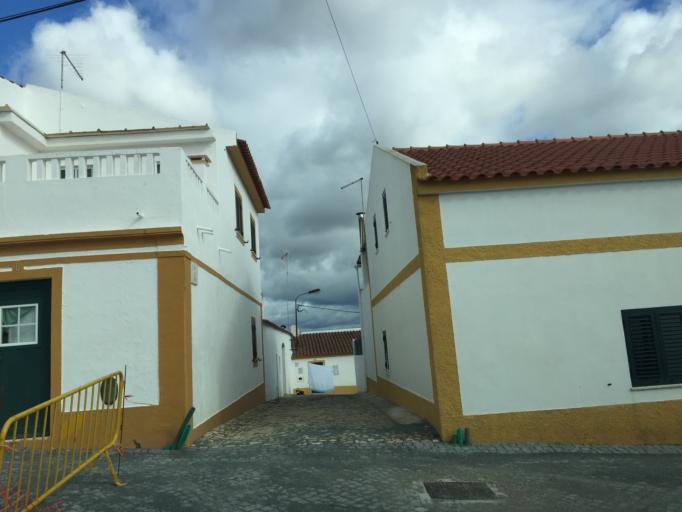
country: PT
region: Portalegre
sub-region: Alter do Chao
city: Alter do Chao
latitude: 39.2022
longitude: -7.6593
